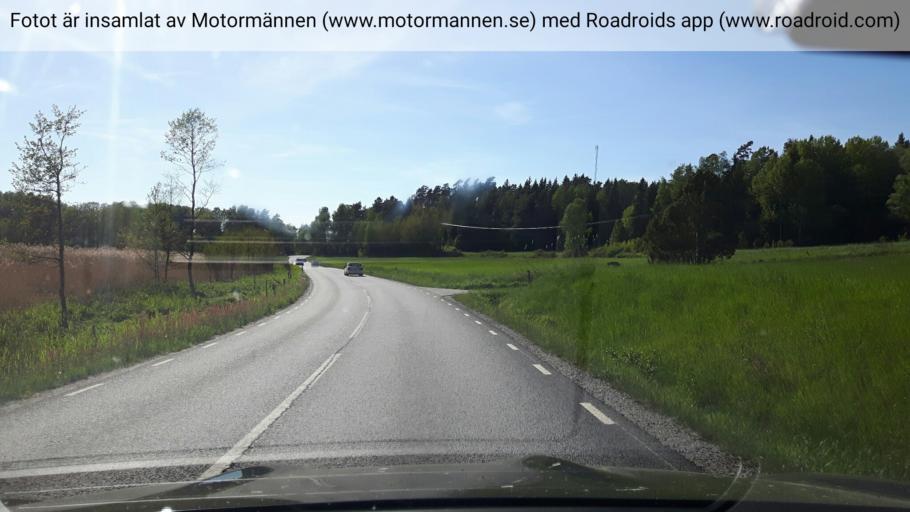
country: SE
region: Stockholm
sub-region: Norrtalje Kommun
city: Norrtalje
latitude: 59.6796
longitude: 18.7175
